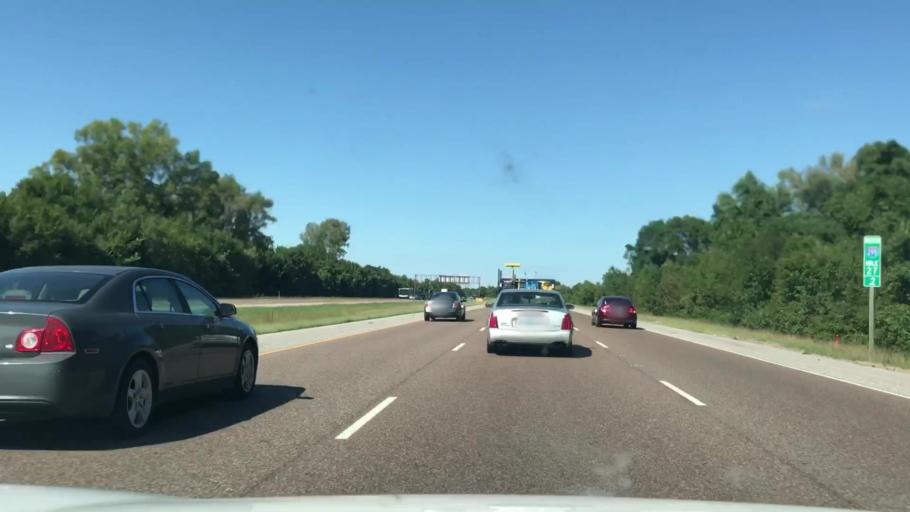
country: US
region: Illinois
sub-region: Madison County
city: Collinsville
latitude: 38.7081
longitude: -90.0276
